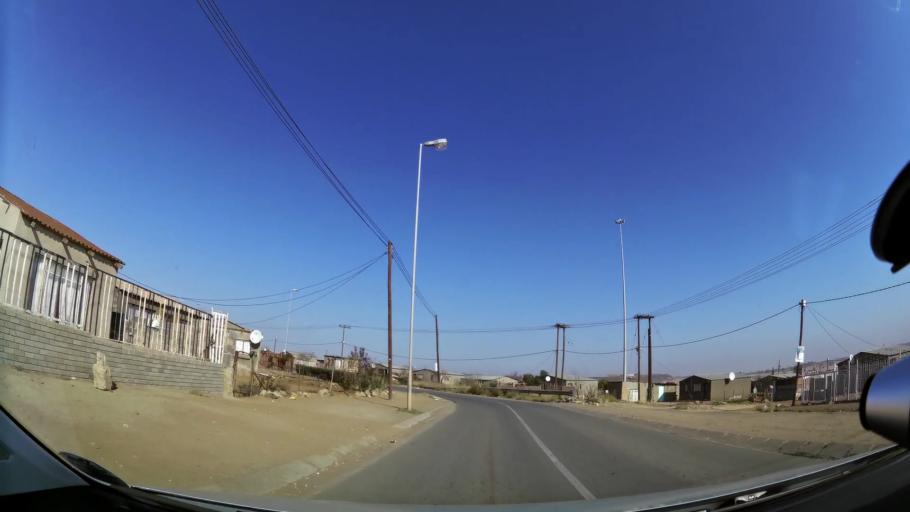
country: ZA
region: Orange Free State
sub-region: Mangaung Metropolitan Municipality
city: Bloemfontein
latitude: -29.1760
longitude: 26.2257
